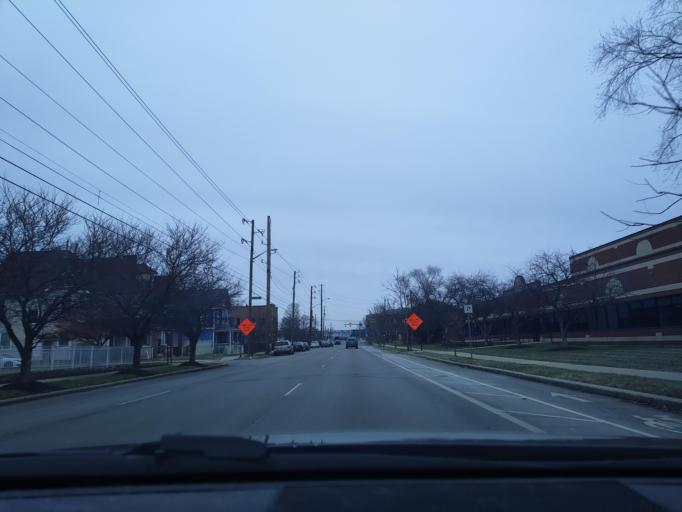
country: US
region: Indiana
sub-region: Marion County
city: Indianapolis
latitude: 39.8005
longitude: -86.1590
